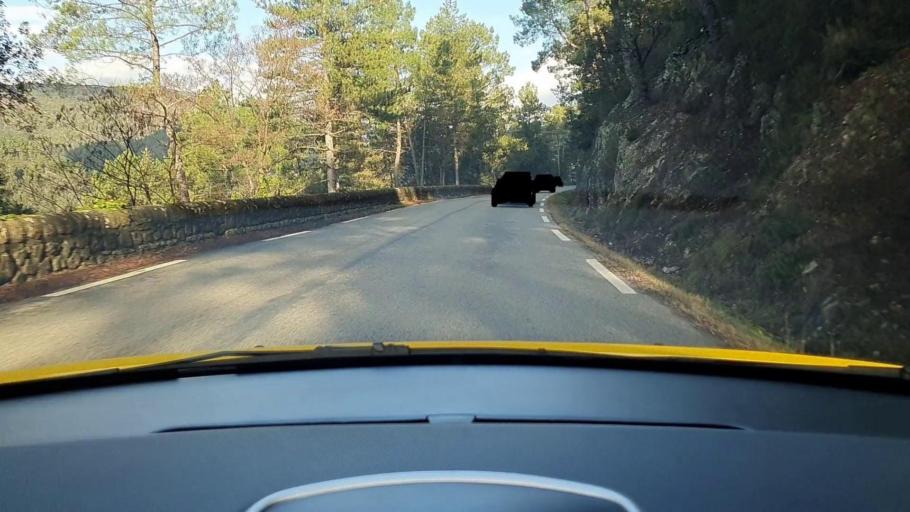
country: FR
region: Languedoc-Roussillon
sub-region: Departement du Gard
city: Branoux-les-Taillades
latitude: 44.3195
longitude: 3.9636
